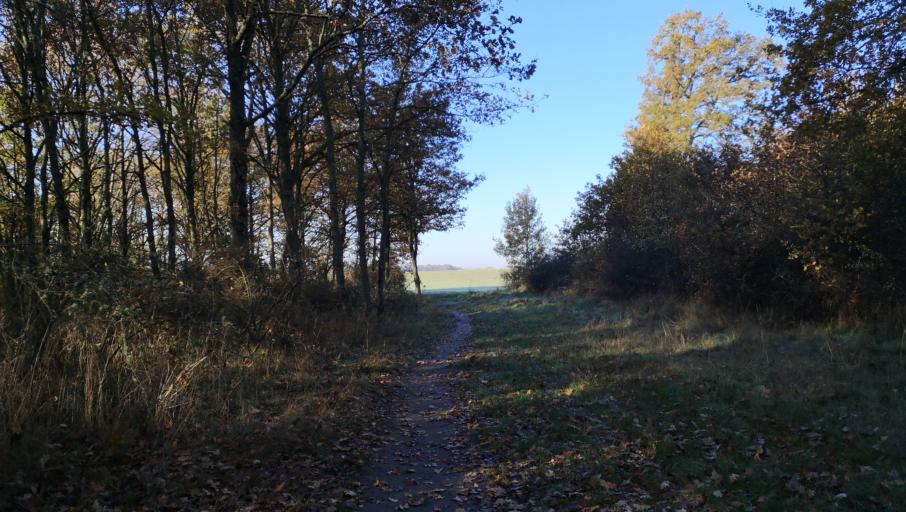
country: FR
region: Centre
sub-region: Departement du Loiret
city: Saran
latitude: 47.9417
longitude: 1.8597
